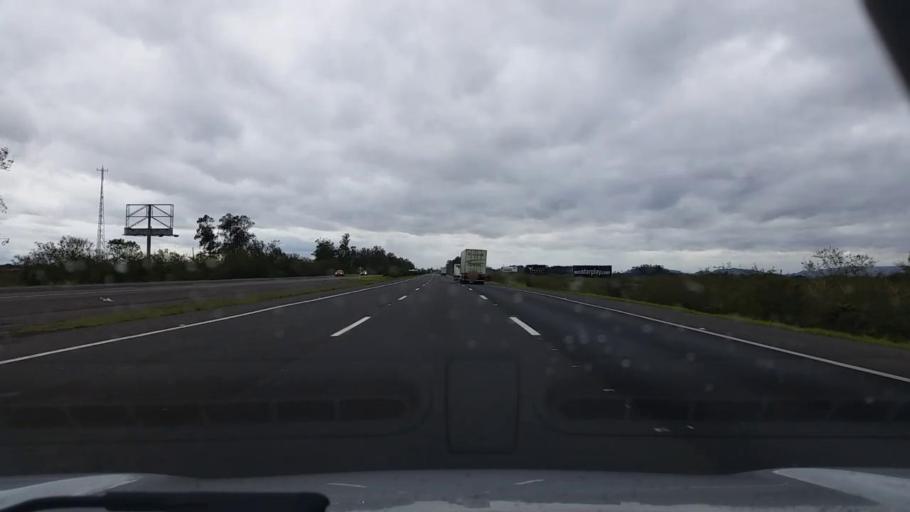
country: BR
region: Rio Grande do Sul
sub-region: Rolante
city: Rolante
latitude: -29.8867
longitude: -50.6652
